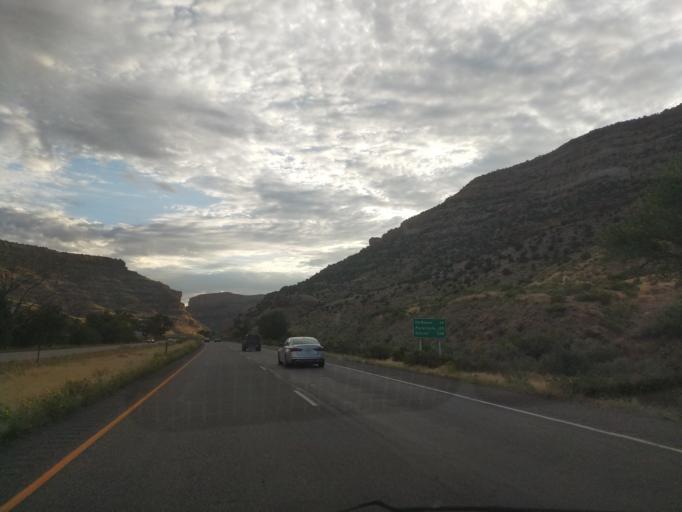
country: US
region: Colorado
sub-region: Mesa County
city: Palisade
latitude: 39.1691
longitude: -108.2969
